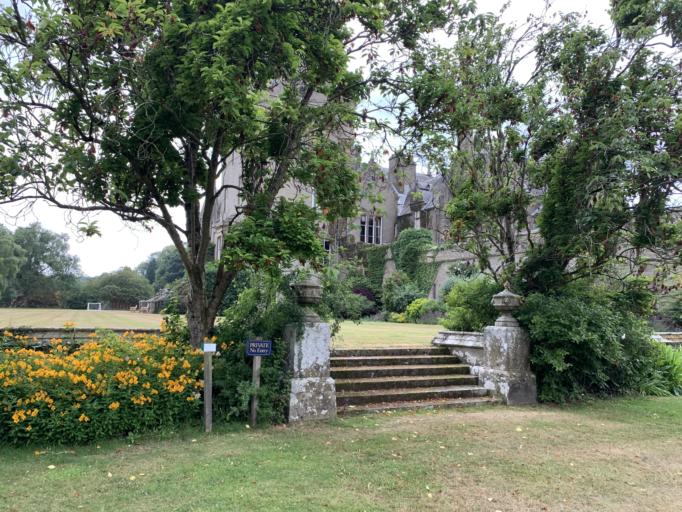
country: GB
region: Scotland
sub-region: Dumfries and Galloway
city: Stranraer
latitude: 54.9145
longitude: -4.9548
